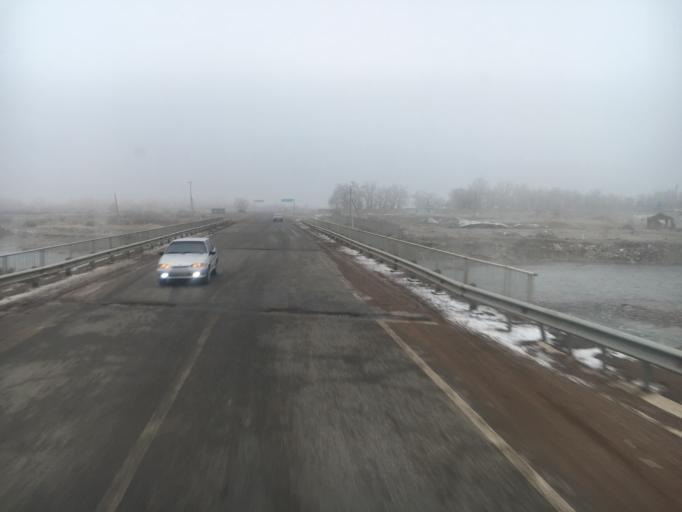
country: KZ
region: Zhambyl
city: Sarykemer
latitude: 43.0402
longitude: 71.5370
